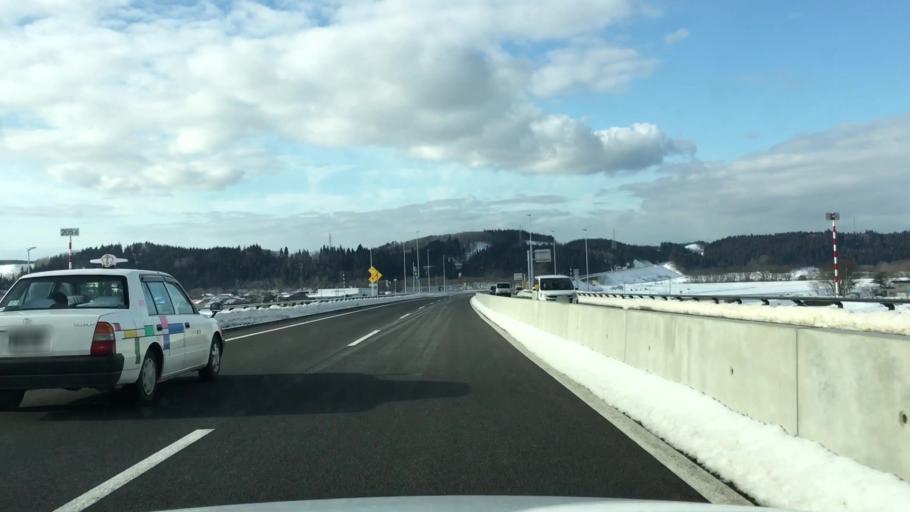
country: JP
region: Akita
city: Takanosu
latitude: 40.2016
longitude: 140.3951
